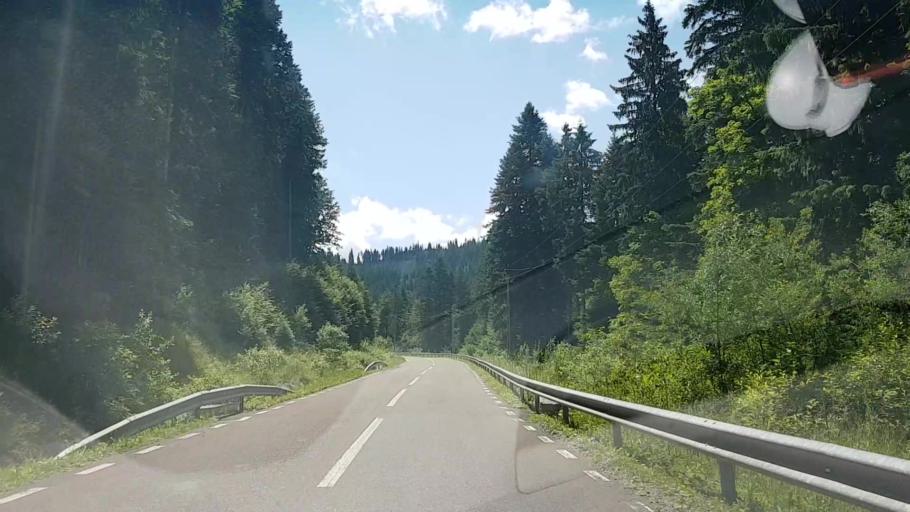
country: RO
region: Suceava
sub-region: Comuna Sadova
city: Sadova
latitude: 47.4707
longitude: 25.5126
